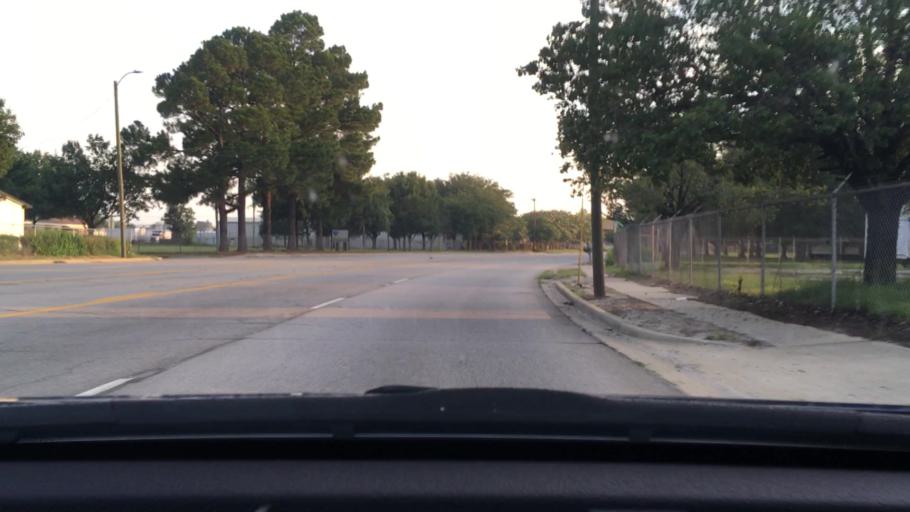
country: US
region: South Carolina
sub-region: Sumter County
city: Sumter
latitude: 33.9111
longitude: -80.3376
